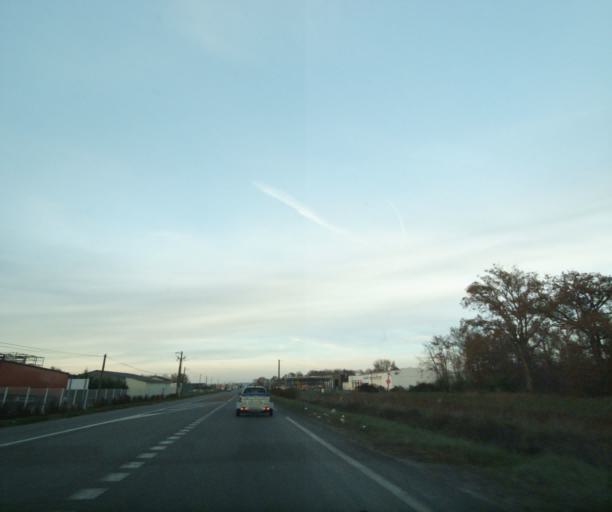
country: FR
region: Aquitaine
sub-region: Departement de la Gironde
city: Langon
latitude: 44.5182
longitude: -0.2397
